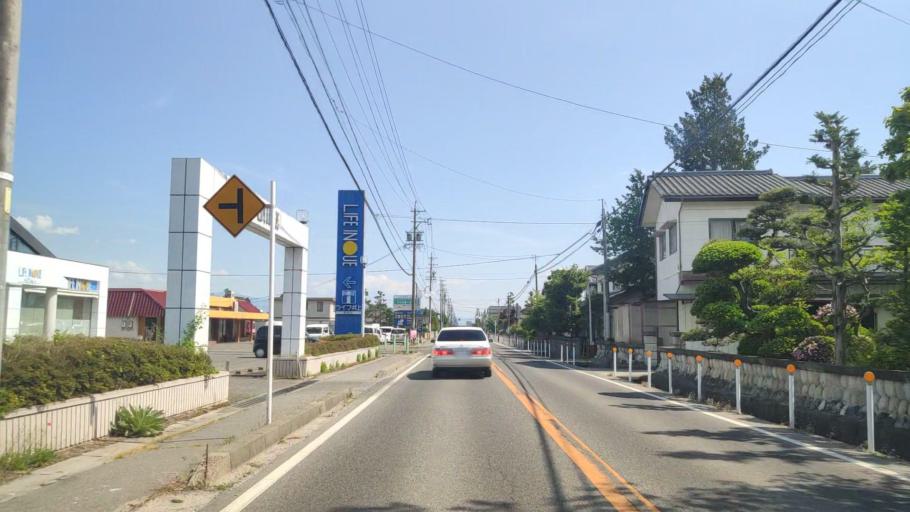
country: JP
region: Nagano
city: Hotaka
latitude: 36.3704
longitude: 137.8748
